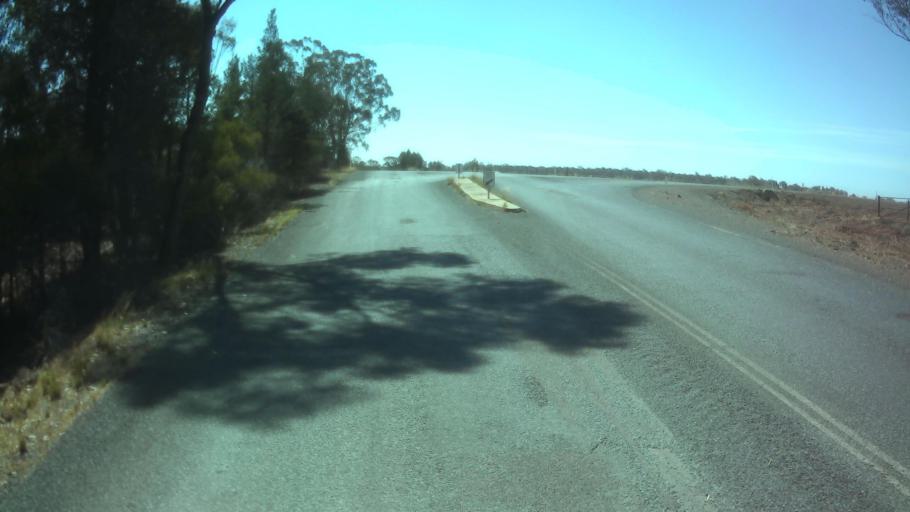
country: AU
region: New South Wales
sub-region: Weddin
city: Grenfell
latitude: -33.7568
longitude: 147.8554
